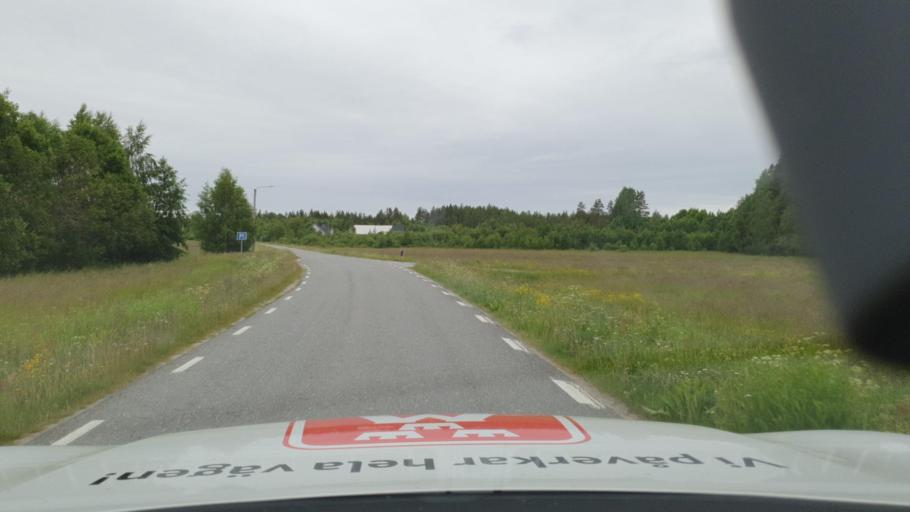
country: SE
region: Vaesterbotten
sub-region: Nordmalings Kommun
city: Nordmaling
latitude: 63.5017
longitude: 19.4174
